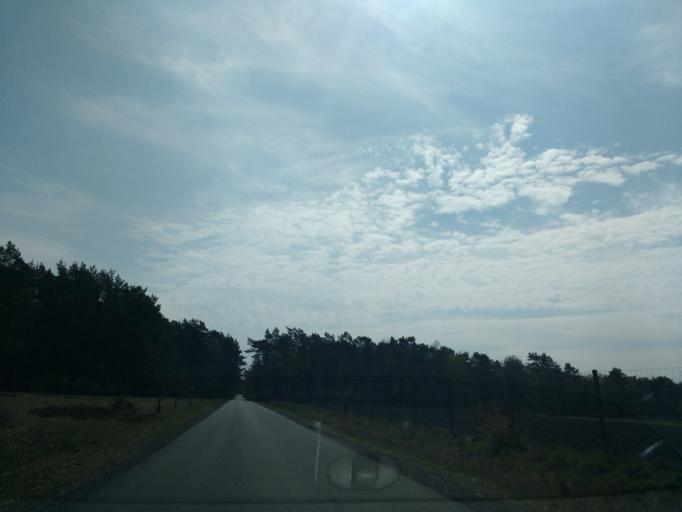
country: DE
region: North Rhine-Westphalia
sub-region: Regierungsbezirk Detmold
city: Hovelhof
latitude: 51.8433
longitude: 8.6839
